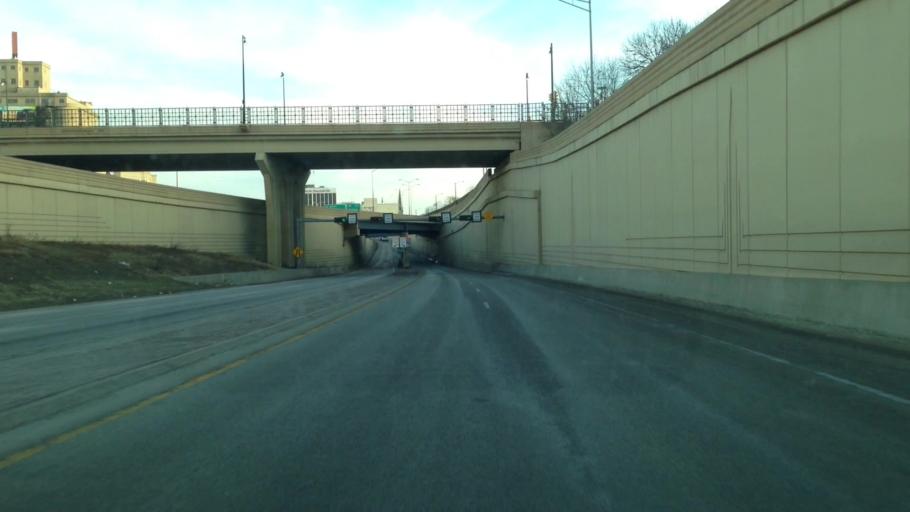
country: US
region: Wisconsin
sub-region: Milwaukee County
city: Milwaukee
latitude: 43.0495
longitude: -87.9267
